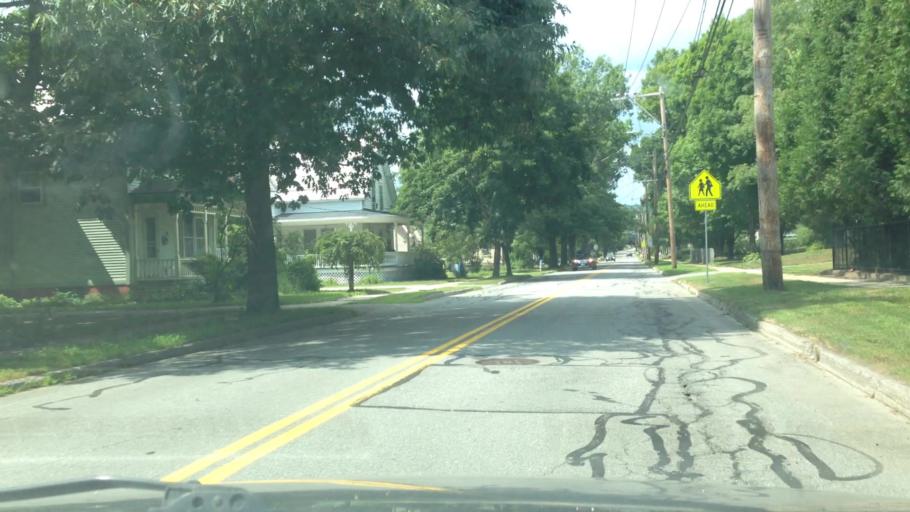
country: US
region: New Hampshire
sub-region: Cheshire County
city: Keene
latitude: 42.9319
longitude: -72.2663
